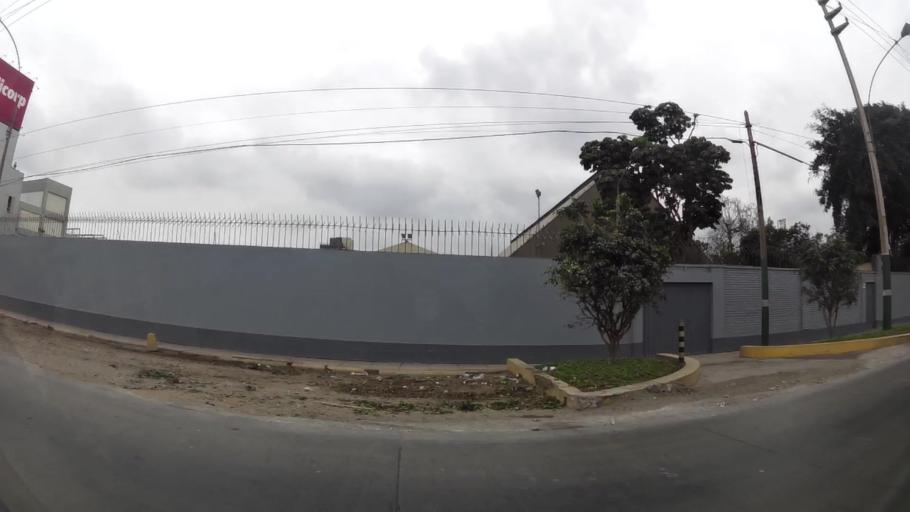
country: PE
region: Callao
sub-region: Callao
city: Callao
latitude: -12.0481
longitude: -77.0955
